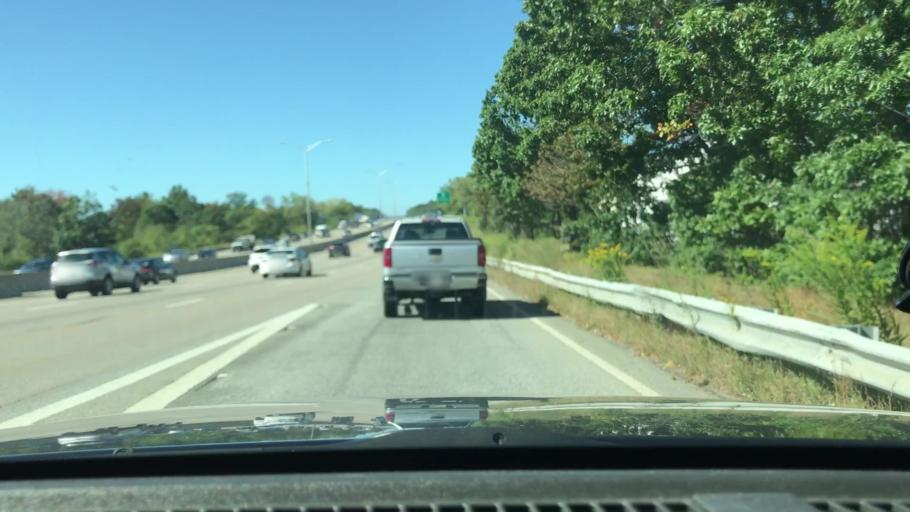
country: US
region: Massachusetts
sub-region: Middlesex County
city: Woburn
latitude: 42.5027
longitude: -71.1317
